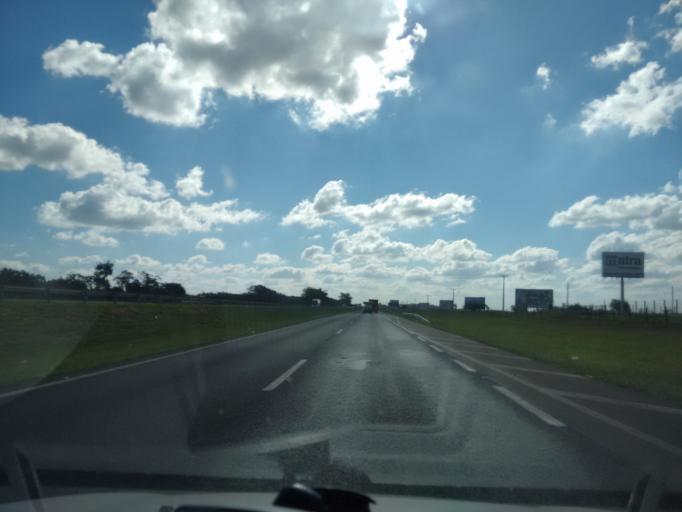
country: BR
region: Sao Paulo
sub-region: Ibate
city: Ibate
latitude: -21.9344
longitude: -48.0151
